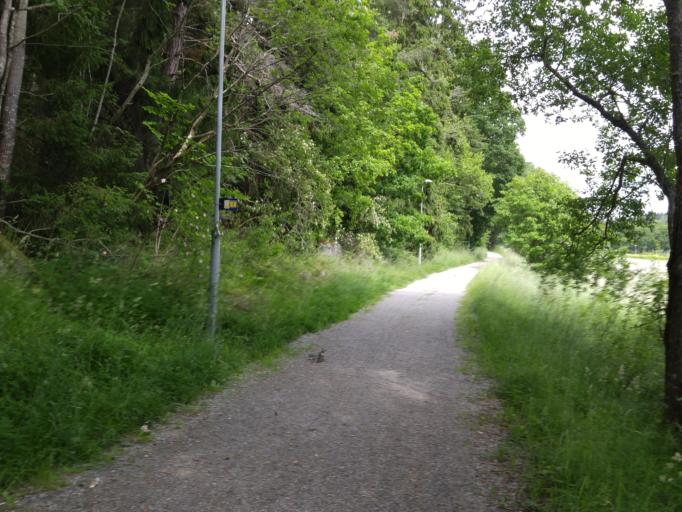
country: SE
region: Stockholm
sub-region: Sigtuna Kommun
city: Sigtuna
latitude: 59.6175
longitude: 17.7057
